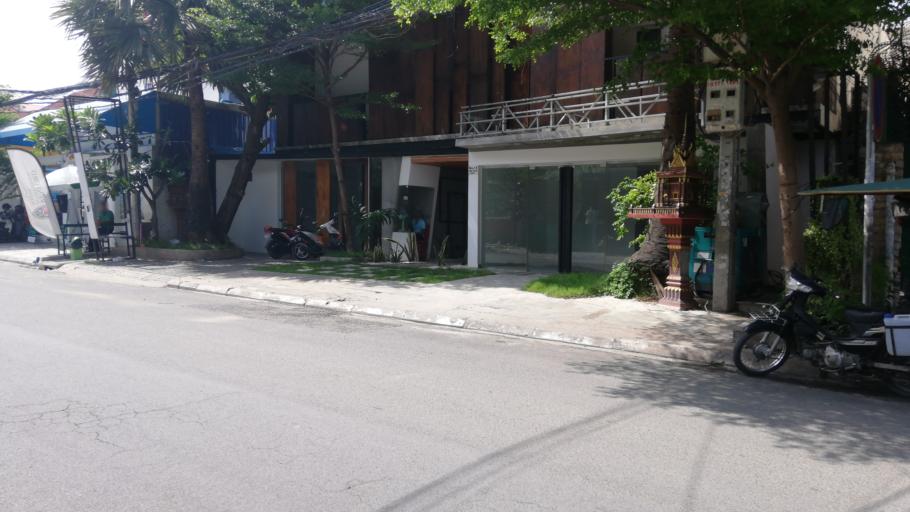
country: KH
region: Phnom Penh
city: Phnom Penh
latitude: 11.5518
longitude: 104.9269
